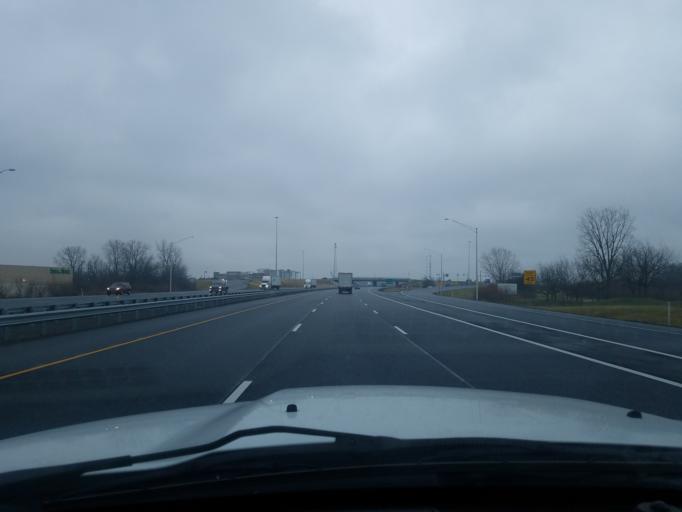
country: US
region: Indiana
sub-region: Hancock County
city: McCordsville
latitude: 39.9895
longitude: -85.9298
